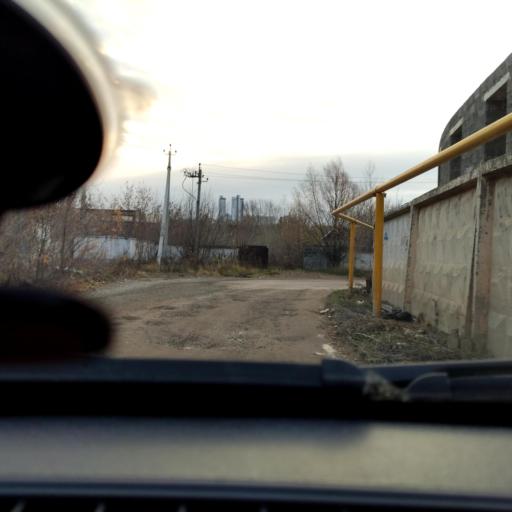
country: RU
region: Bashkortostan
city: Ufa
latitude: 54.7477
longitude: 55.9232
